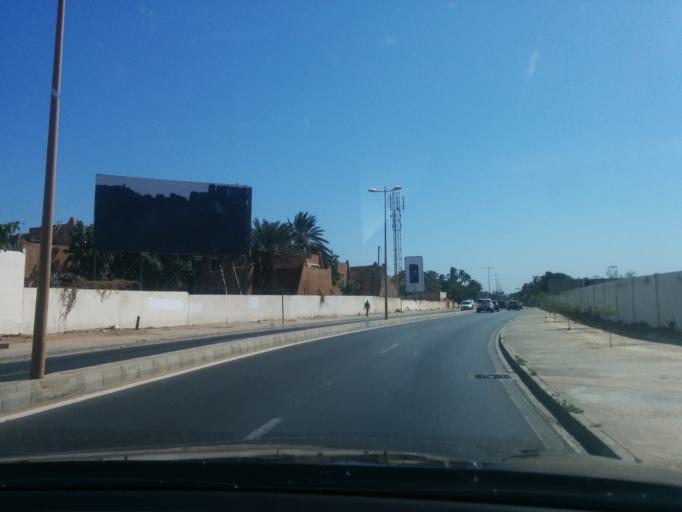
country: SN
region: Dakar
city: Mermoz Boabab
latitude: 14.7047
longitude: -17.4812
